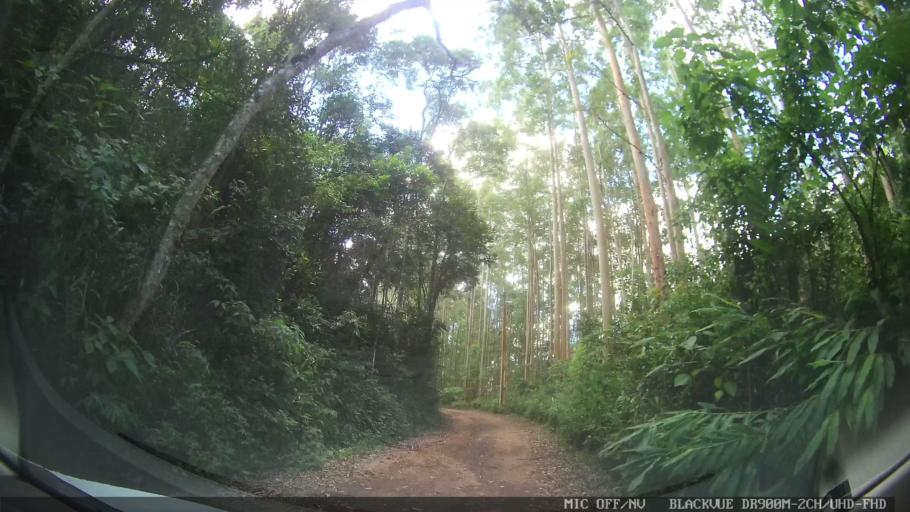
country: BR
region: Minas Gerais
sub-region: Extrema
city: Extrema
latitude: -22.8823
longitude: -46.2939
